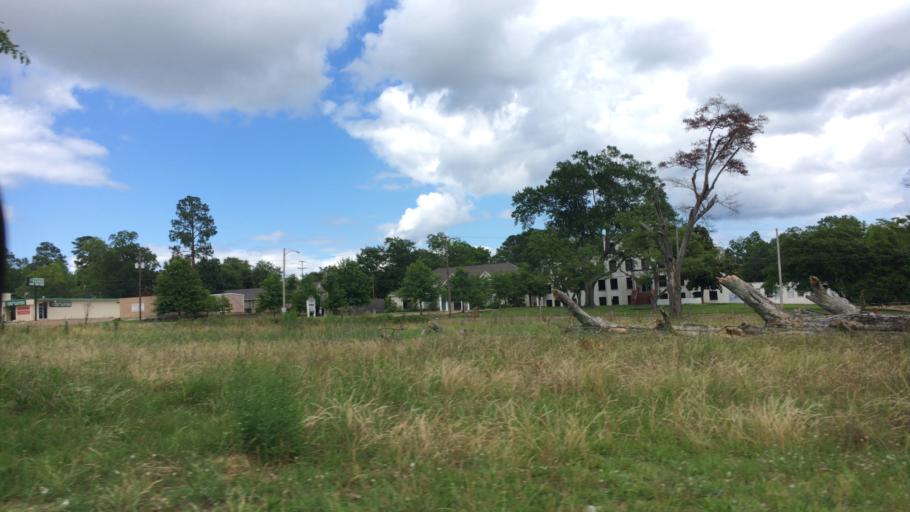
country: US
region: Louisiana
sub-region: Lincoln Parish
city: Ruston
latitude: 32.5211
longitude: -92.6395
